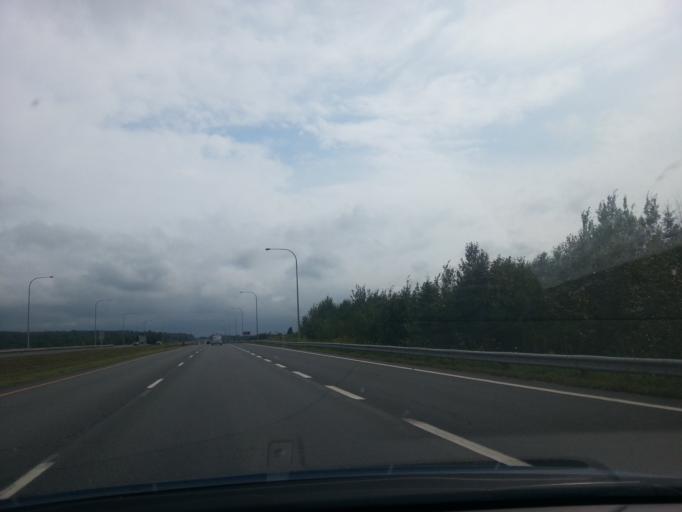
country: US
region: Maine
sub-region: Aroostook County
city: Houlton
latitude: 46.1522
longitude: -67.6092
